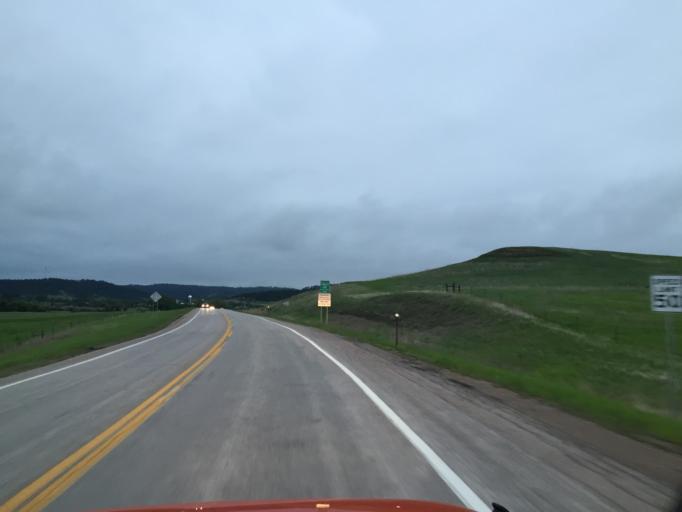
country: US
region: South Dakota
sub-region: Pennington County
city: Colonial Pine Hills
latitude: 43.8366
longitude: -103.2012
